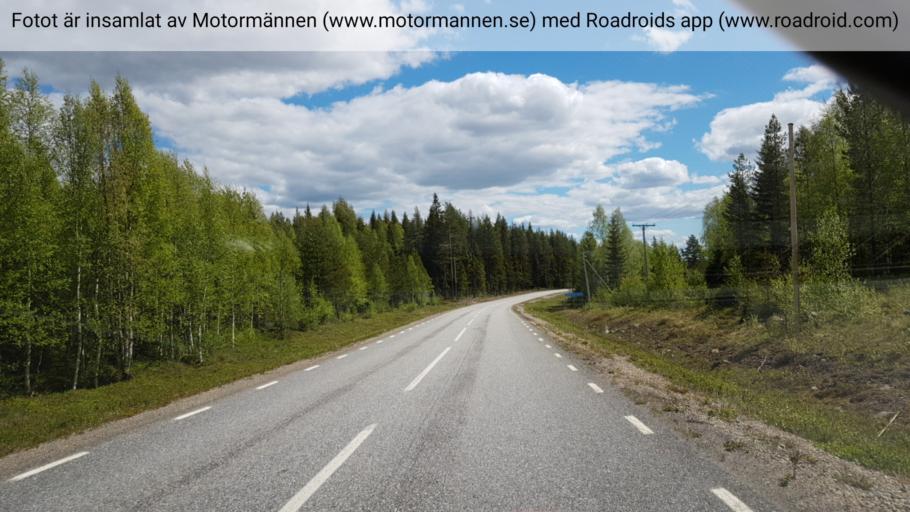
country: SE
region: Vaesterbotten
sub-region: Skelleftea Kommun
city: Langsele
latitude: 64.6905
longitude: 20.0222
